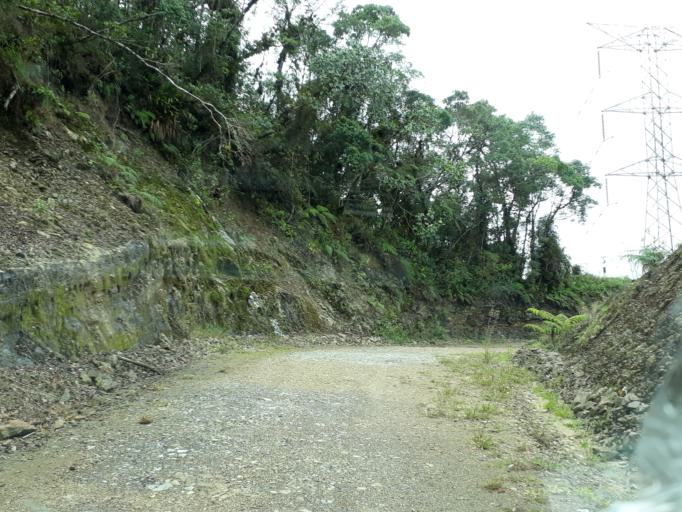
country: CO
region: Cundinamarca
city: Gachala
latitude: 4.7136
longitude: -73.3885
